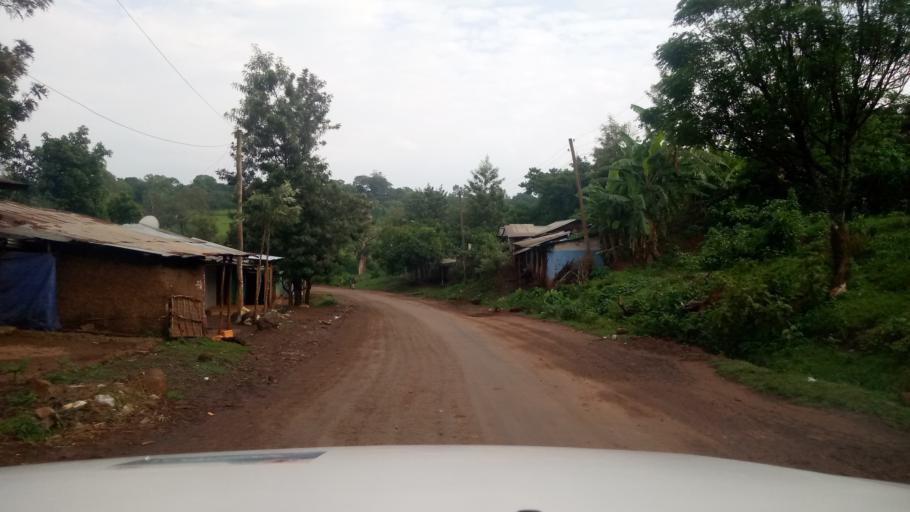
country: ET
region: Oromiya
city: Agaro
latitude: 7.8363
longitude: 36.6776
